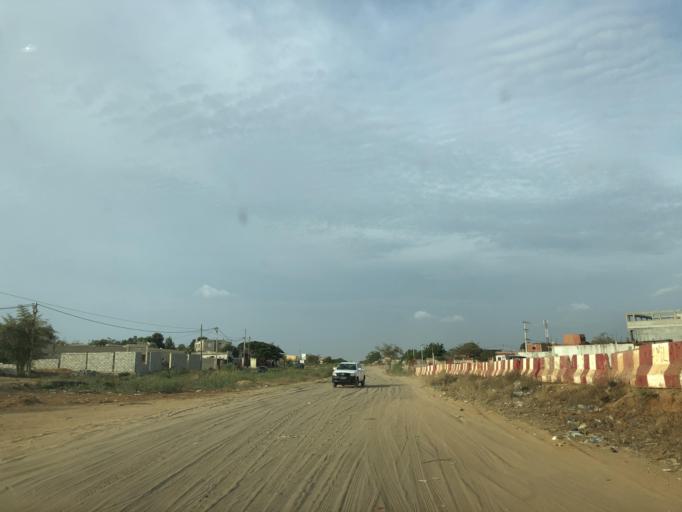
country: AO
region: Luanda
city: Luanda
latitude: -8.9183
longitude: 13.3100
